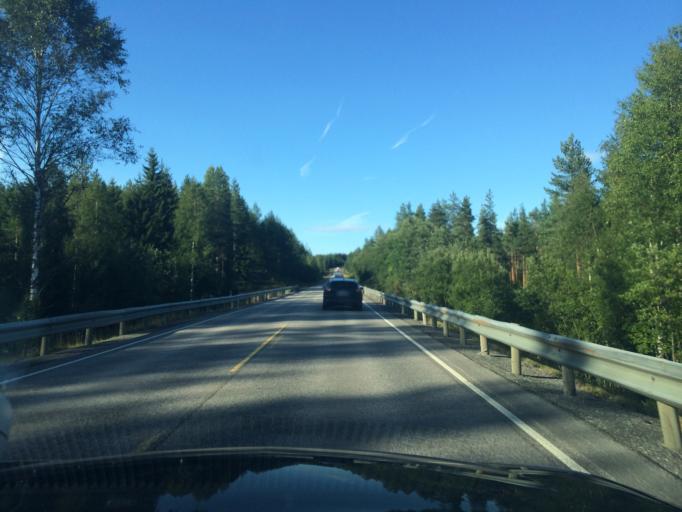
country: NO
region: Hedmark
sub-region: Elverum
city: Elverum
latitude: 60.9503
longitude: 11.6982
